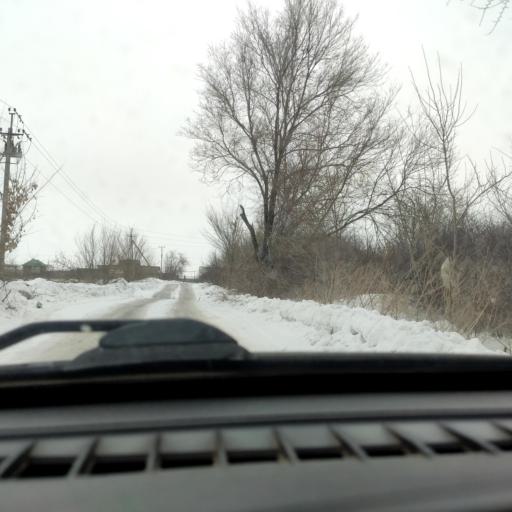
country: RU
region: Samara
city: Tol'yatti
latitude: 53.5685
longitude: 49.4750
